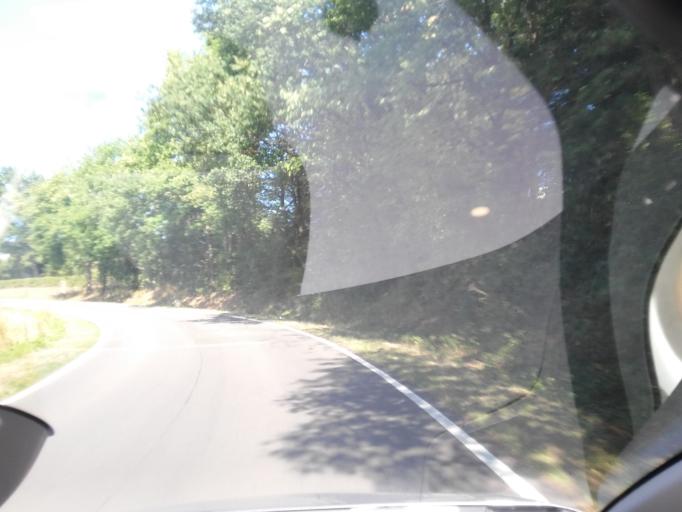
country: DE
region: Saarland
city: Orscholz
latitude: 49.4831
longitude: 6.5448
